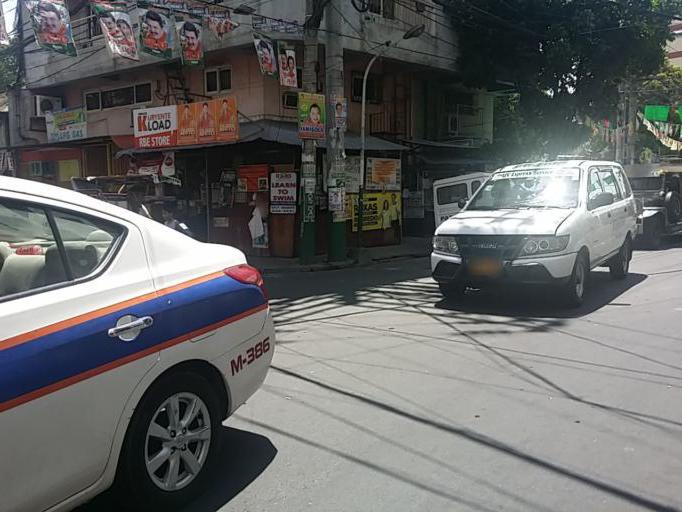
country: PH
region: Metro Manila
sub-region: City of Manila
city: Quiapo
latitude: 14.6005
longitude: 120.9873
